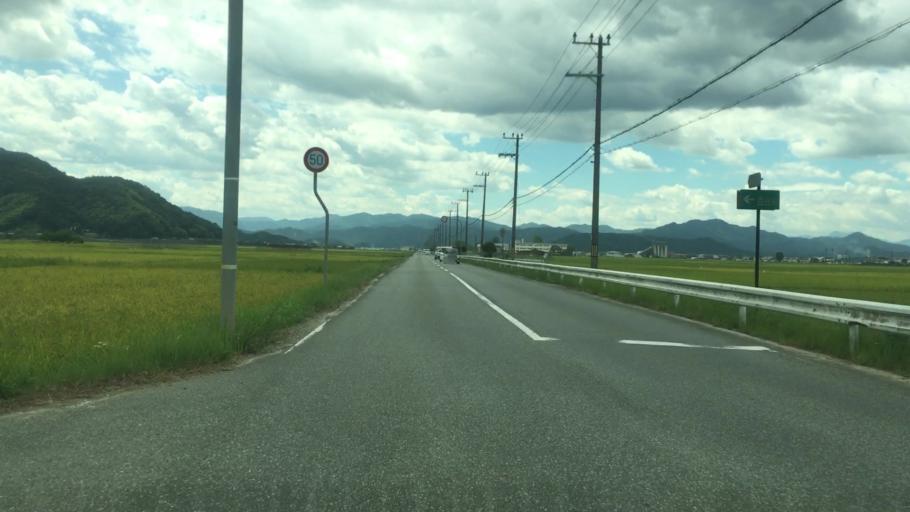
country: JP
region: Hyogo
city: Toyooka
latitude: 35.5402
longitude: 134.8396
